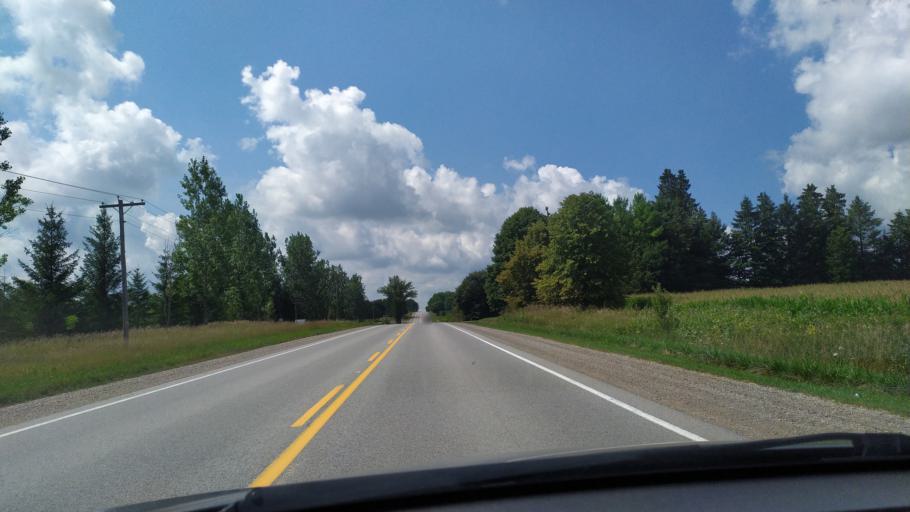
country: CA
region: Ontario
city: South Huron
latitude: 43.3159
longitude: -81.3204
